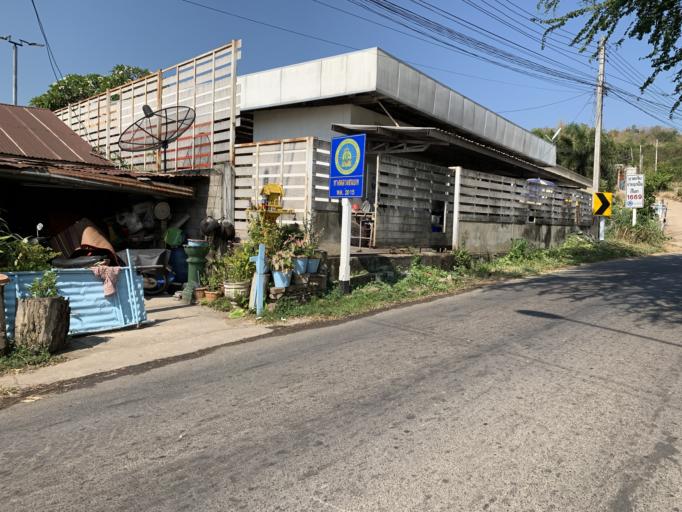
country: TH
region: Phitsanulok
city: Wang Thong
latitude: 16.8437
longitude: 100.5400
